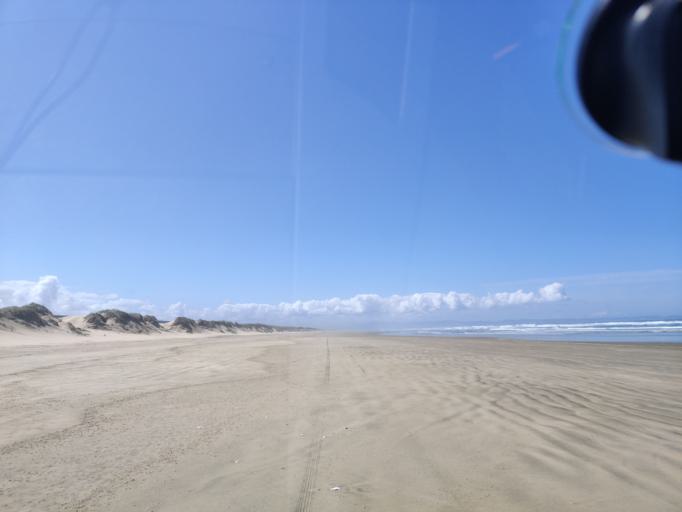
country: NZ
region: Northland
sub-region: Far North District
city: Kaitaia
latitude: -34.9395
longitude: 173.1142
